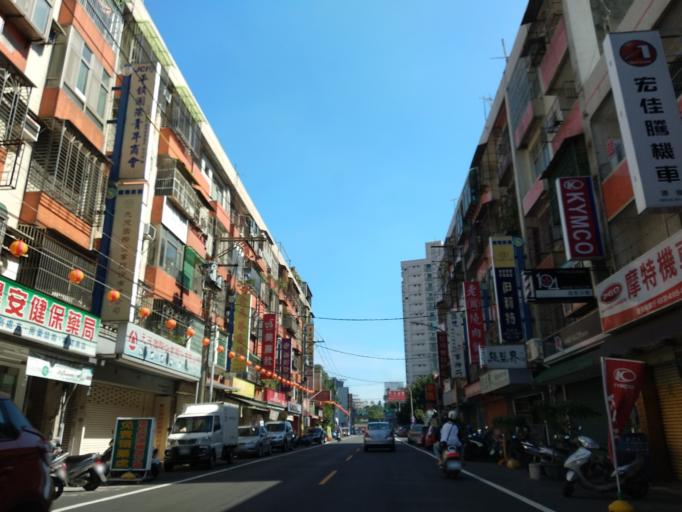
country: TW
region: Taiwan
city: Taoyuan City
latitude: 24.9462
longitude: 121.2140
